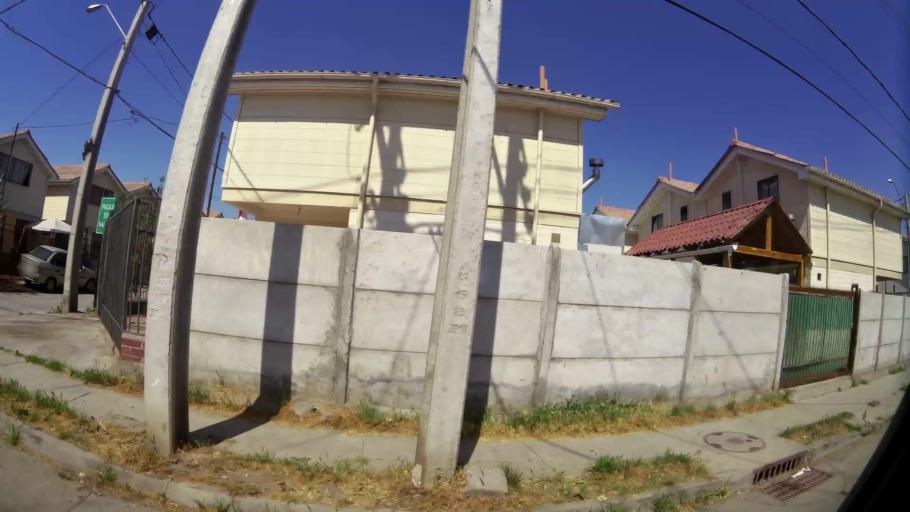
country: CL
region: Santiago Metropolitan
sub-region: Provincia de Talagante
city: Penaflor
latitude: -33.5736
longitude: -70.8059
